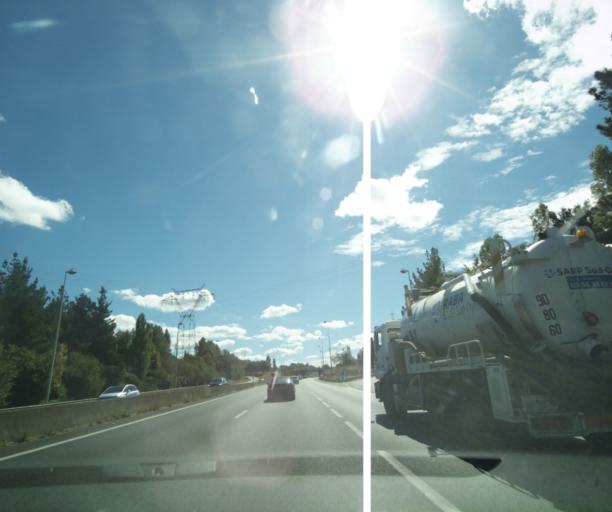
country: FR
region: Aquitaine
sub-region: Departement de la Gironde
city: Artigues-pres-Bordeaux
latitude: 44.8461
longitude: -0.5025
